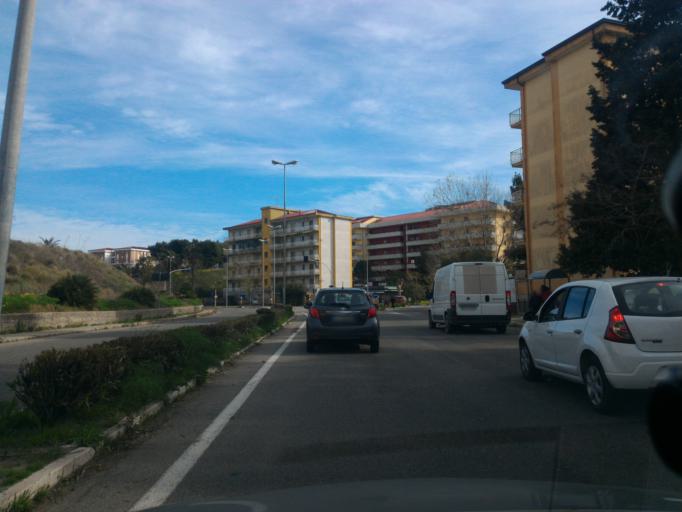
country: IT
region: Calabria
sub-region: Provincia di Crotone
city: Crotone
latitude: 39.0740
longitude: 17.1148
